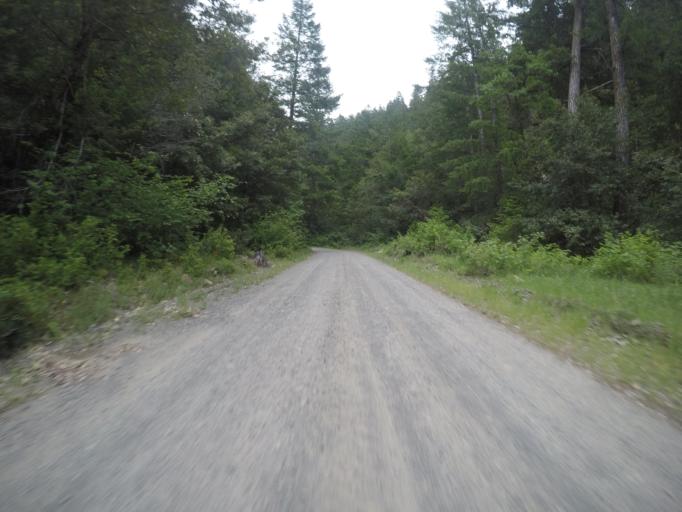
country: US
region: California
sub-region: Del Norte County
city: Bertsch-Oceanview
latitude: 41.7328
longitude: -123.8839
